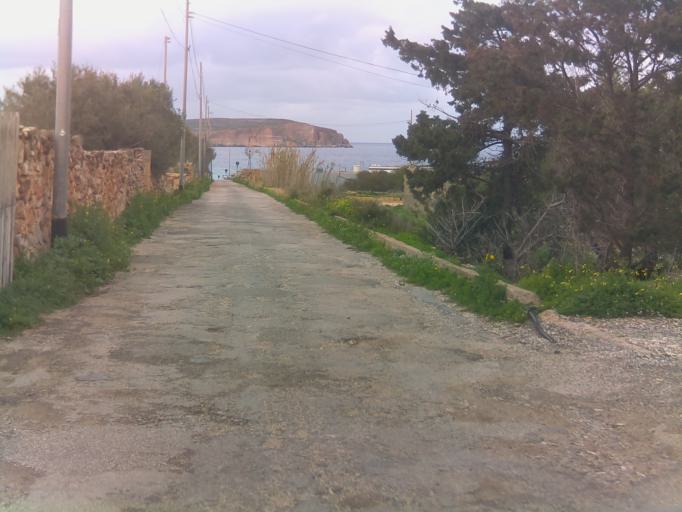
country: MT
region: Il-Mellieha
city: Mellieha
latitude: 35.9863
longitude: 14.3612
